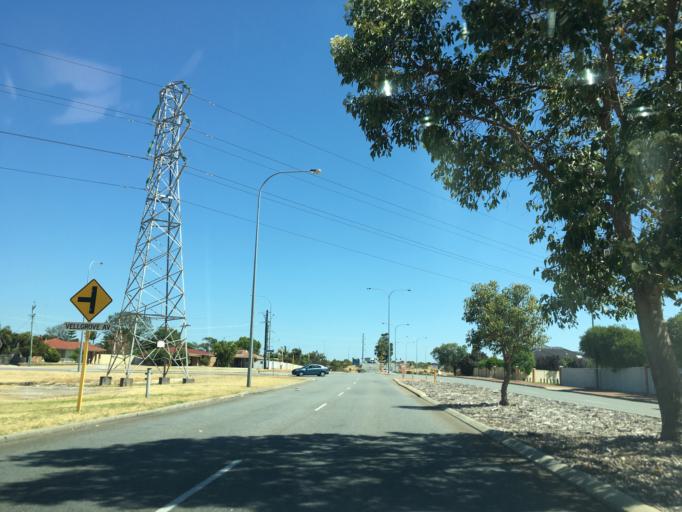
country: AU
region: Western Australia
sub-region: Canning
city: Canning Vale
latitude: -32.0531
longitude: 115.9044
